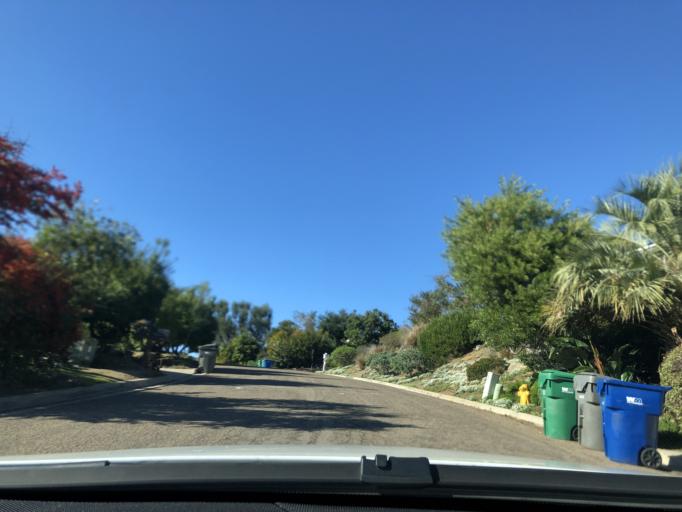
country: US
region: California
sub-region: San Diego County
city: Bostonia
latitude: 32.7816
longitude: -116.9388
